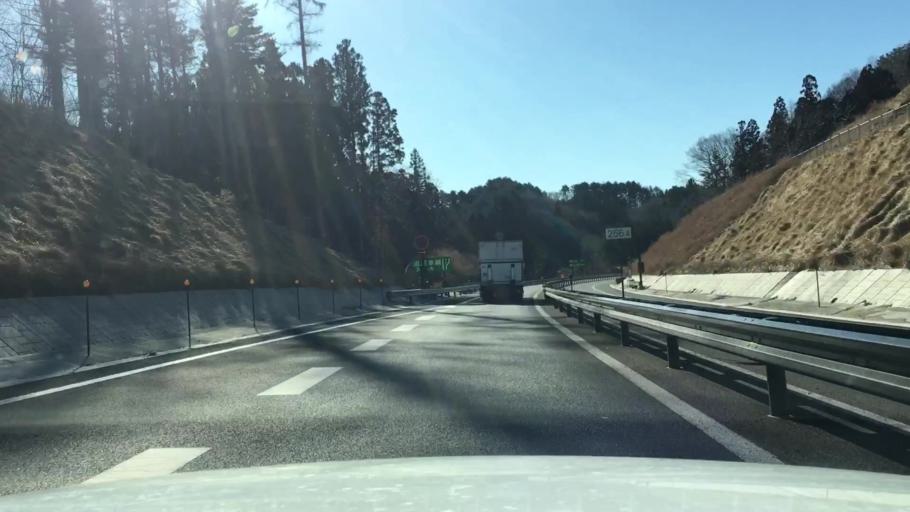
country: JP
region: Iwate
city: Miyako
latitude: 39.5927
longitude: 141.9406
